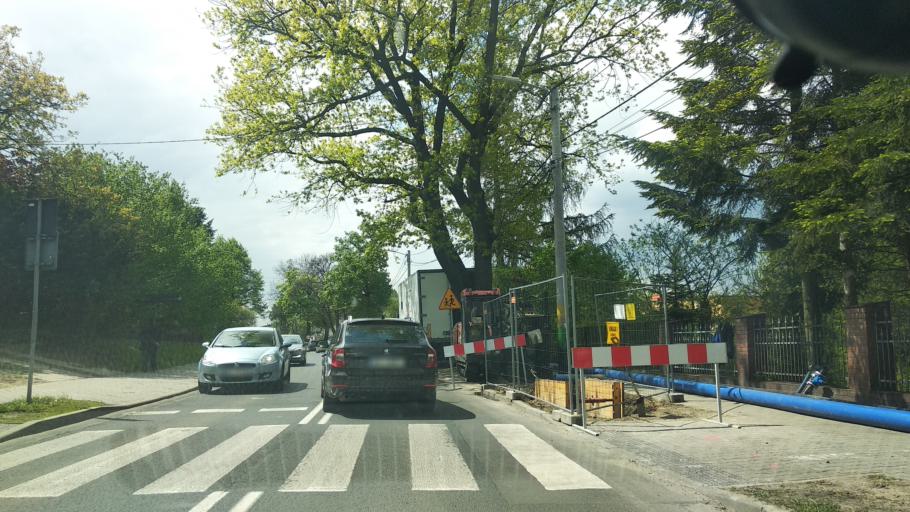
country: PL
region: Silesian Voivodeship
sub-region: Swietochlowice
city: Swietochlowice
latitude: 50.2310
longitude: 18.9518
